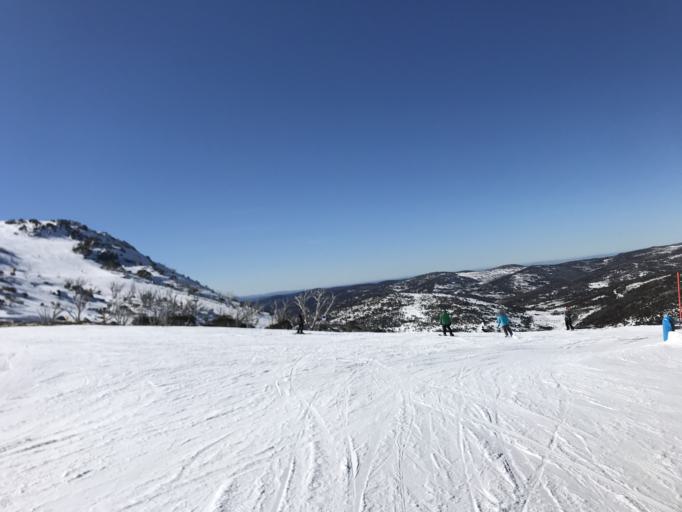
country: AU
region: New South Wales
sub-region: Snowy River
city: Jindabyne
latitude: -36.3828
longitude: 148.3951
